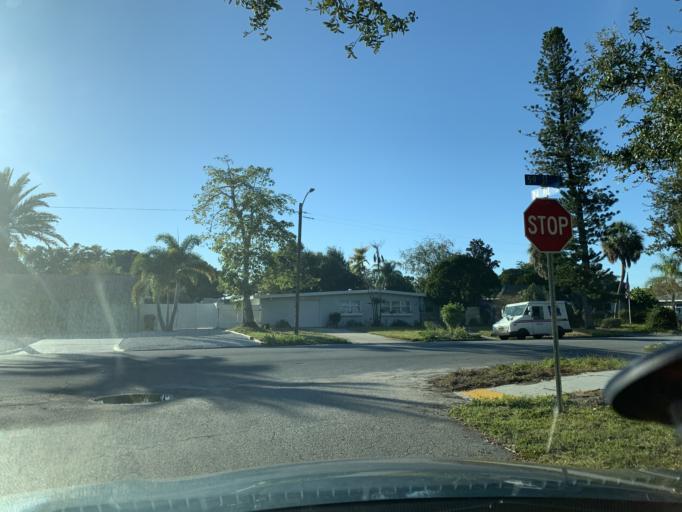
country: US
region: Florida
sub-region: Pinellas County
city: Gulfport
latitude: 27.7464
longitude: -82.7136
